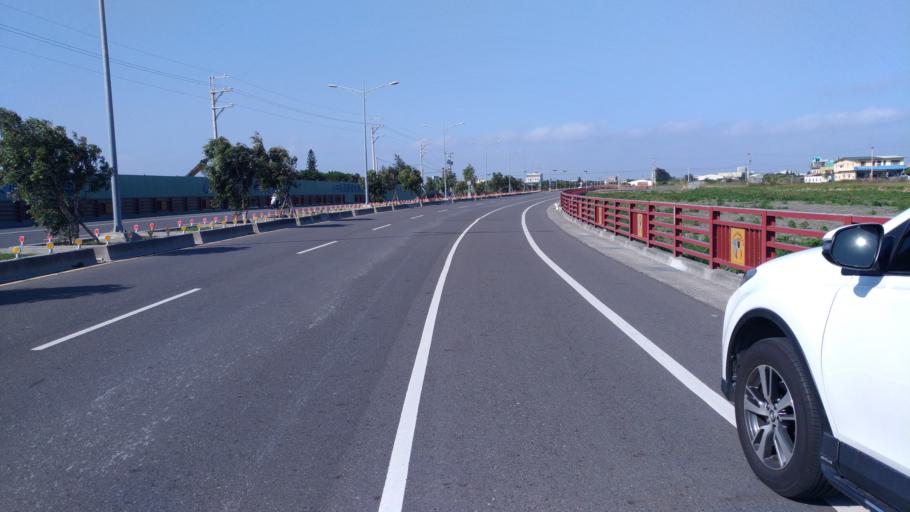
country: TW
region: Taiwan
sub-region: Changhua
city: Chang-hua
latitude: 24.0576
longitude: 120.4241
